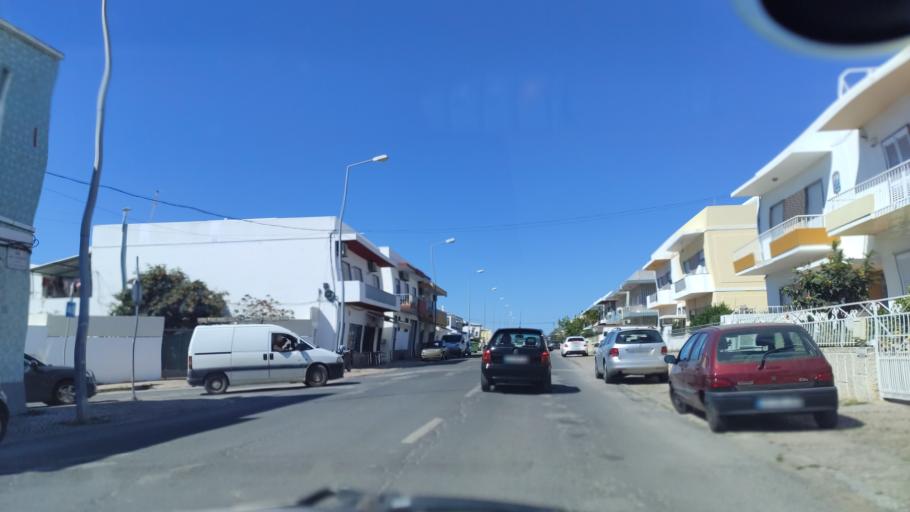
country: PT
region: Faro
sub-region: Olhao
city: Olhao
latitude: 37.0354
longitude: -7.8481
